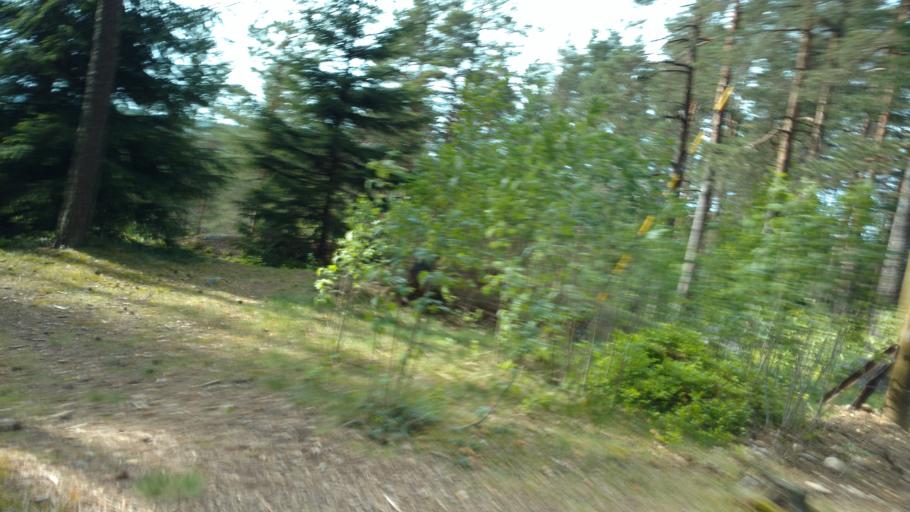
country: FI
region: Varsinais-Suomi
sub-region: Salo
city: Salo
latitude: 60.3844
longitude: 23.1506
